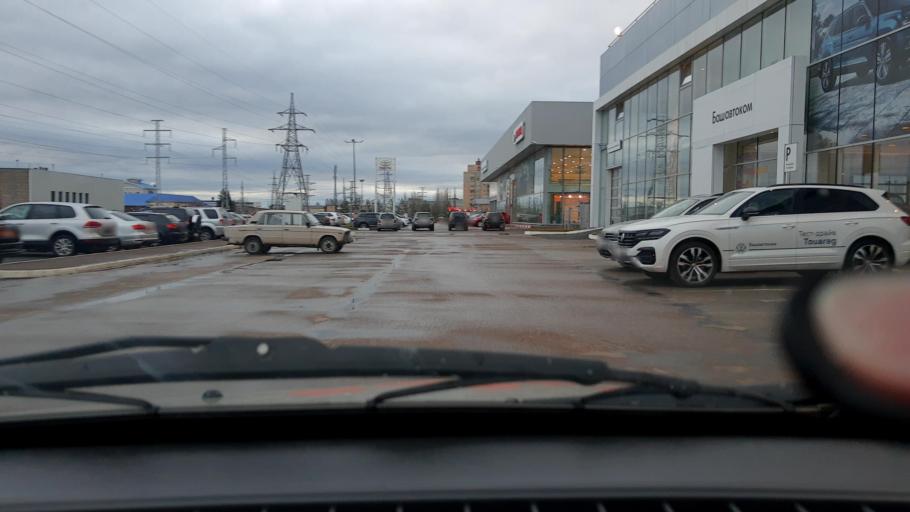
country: RU
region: Bashkortostan
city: Ufa
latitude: 54.8005
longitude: 56.0556
